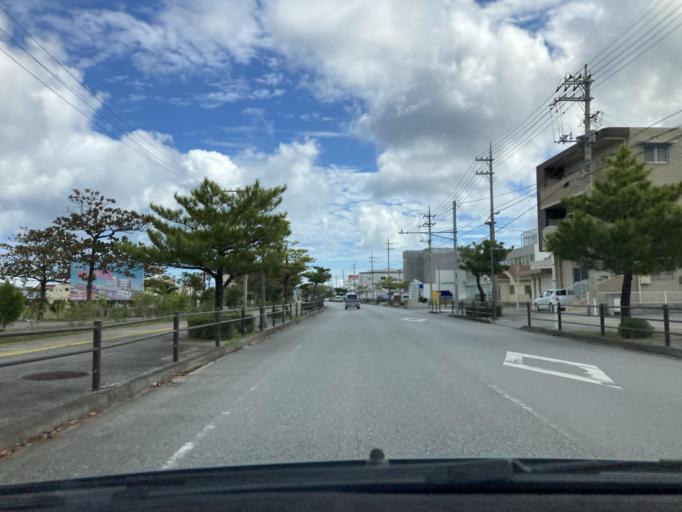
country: JP
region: Okinawa
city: Ginowan
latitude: 26.2075
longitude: 127.7585
